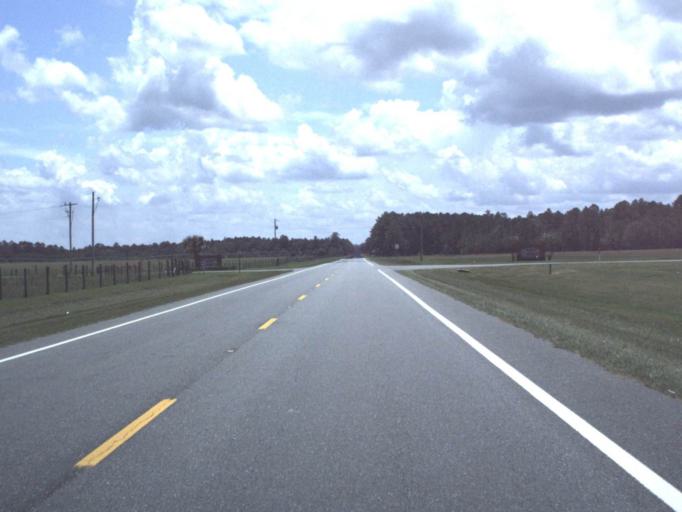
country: US
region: Florida
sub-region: Bradford County
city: Starke
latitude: 30.0493
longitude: -82.1721
